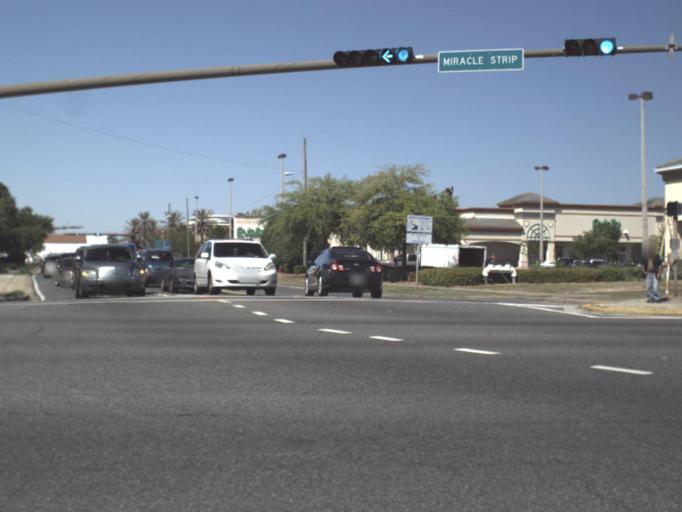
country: US
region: Florida
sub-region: Okaloosa County
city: Fort Walton Beach
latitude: 30.4034
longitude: -86.6041
